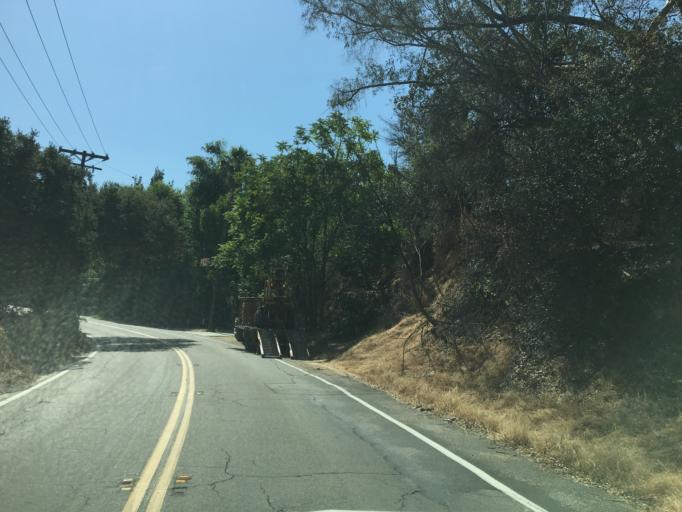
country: US
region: California
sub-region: Los Angeles County
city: Covina
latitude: 34.0746
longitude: -117.8639
